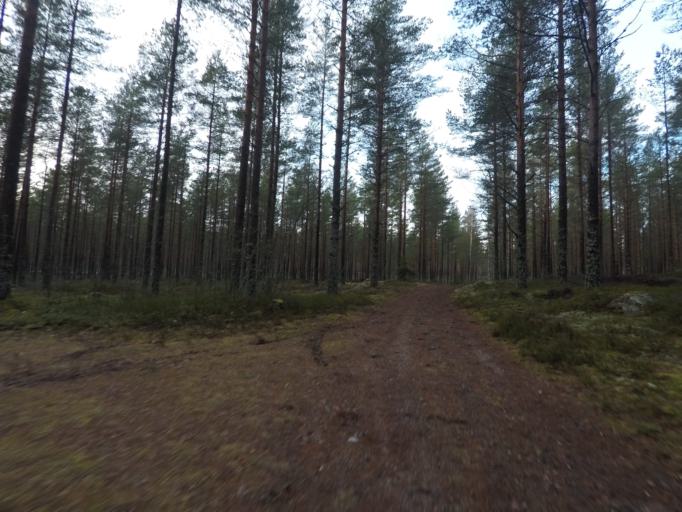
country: SE
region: Vaestmanland
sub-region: Kungsors Kommun
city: Kungsoer
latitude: 59.3517
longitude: 16.1156
